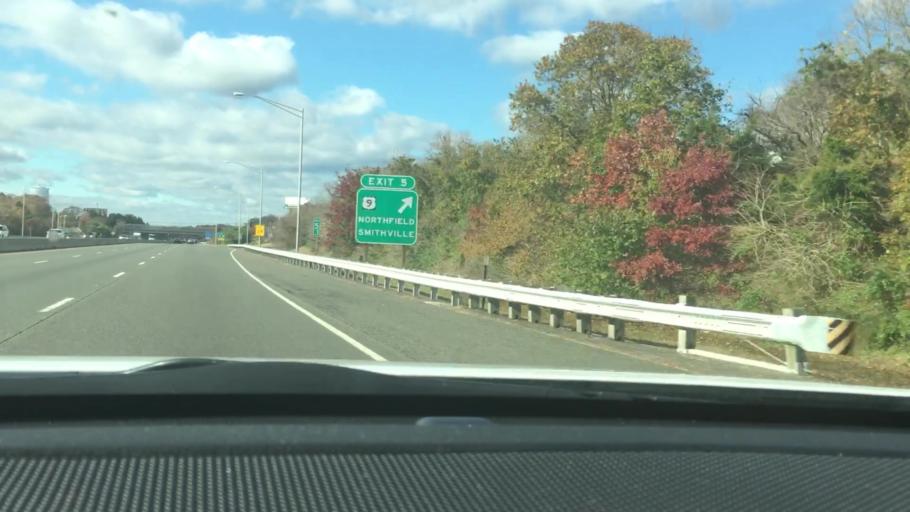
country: US
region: New Jersey
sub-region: Atlantic County
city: Pleasantville
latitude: 39.3996
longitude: -74.5191
